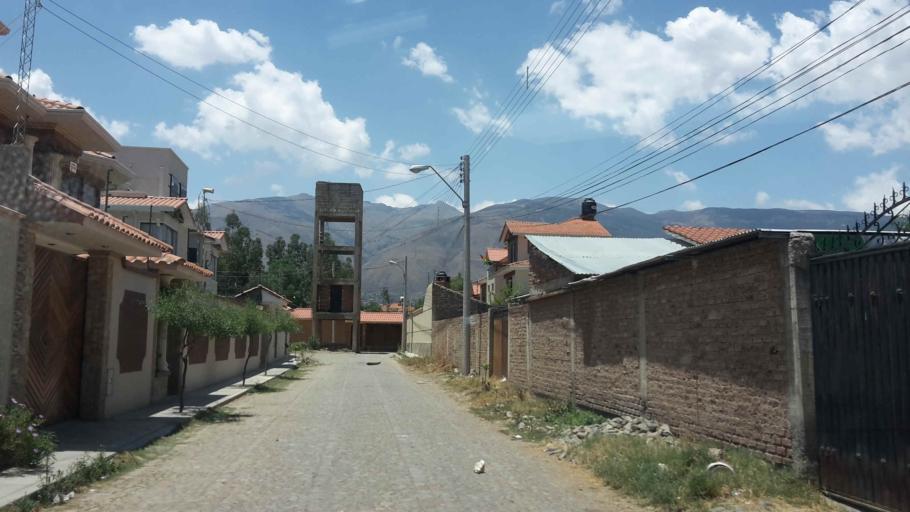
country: BO
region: Cochabamba
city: Cochabamba
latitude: -17.3739
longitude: -66.1975
